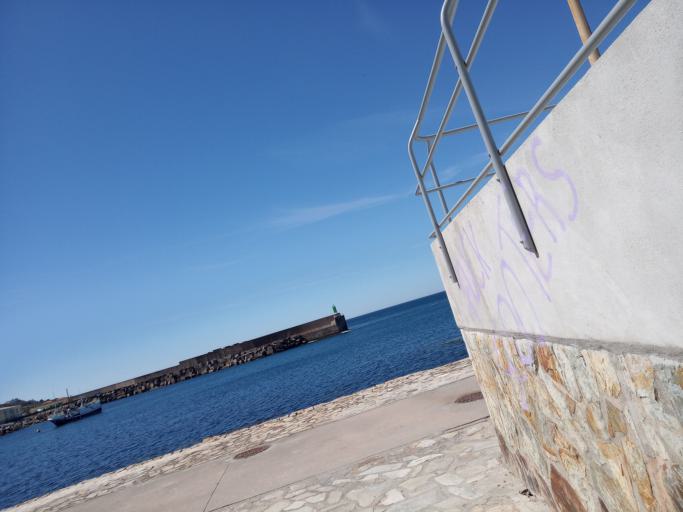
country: ES
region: Galicia
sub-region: Provincia de Pontevedra
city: A Guarda
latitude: 41.9019
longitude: -8.8788
